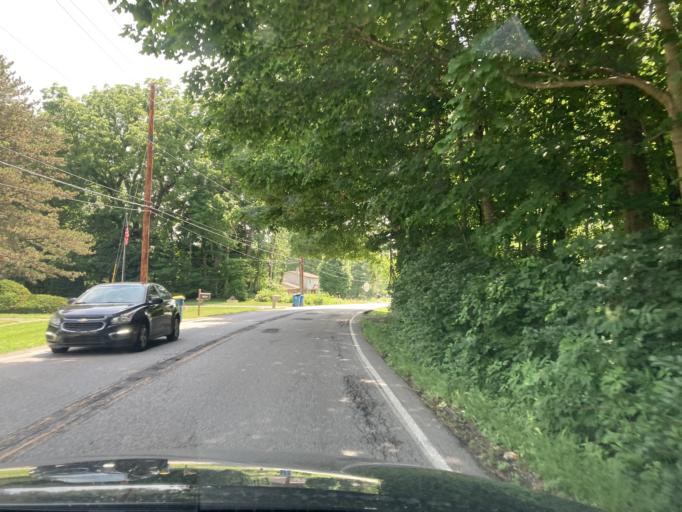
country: US
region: Indiana
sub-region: Marion County
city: Meridian Hills
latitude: 39.8646
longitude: -86.1796
